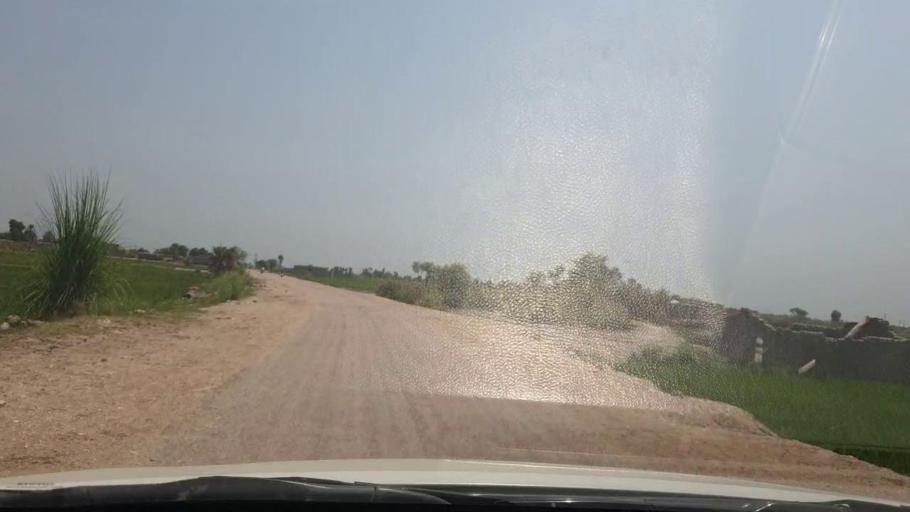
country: PK
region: Sindh
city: Rustam jo Goth
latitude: 28.0287
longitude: 68.7987
